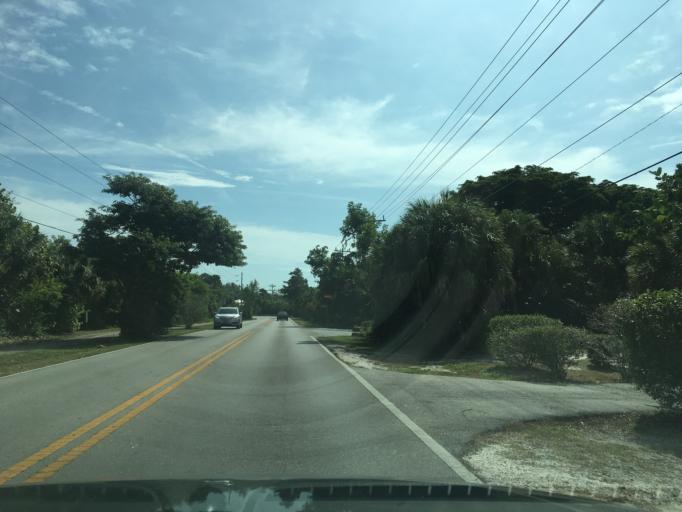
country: US
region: Florida
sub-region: Lee County
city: Saint James City
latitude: 26.4566
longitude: -82.1430
